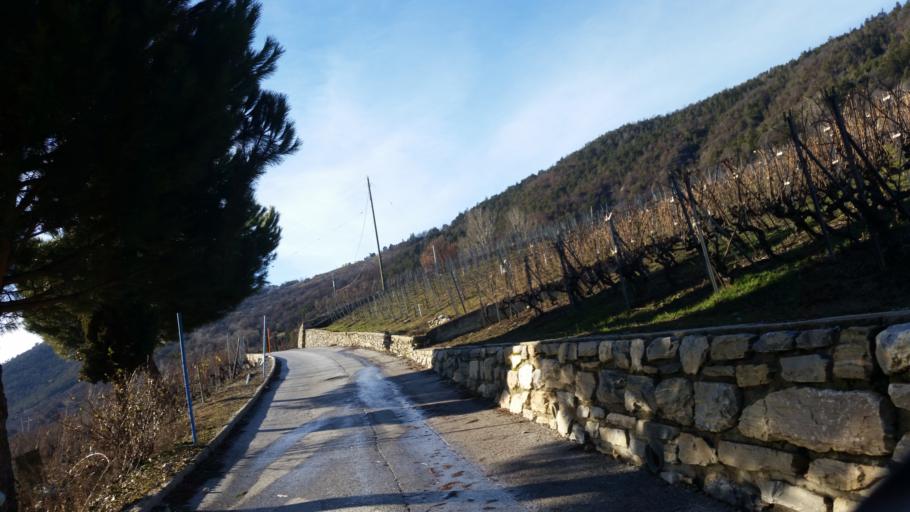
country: CH
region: Valais
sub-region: Sierre District
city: Chermignon-d'en Haut
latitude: 46.2749
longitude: 7.4736
